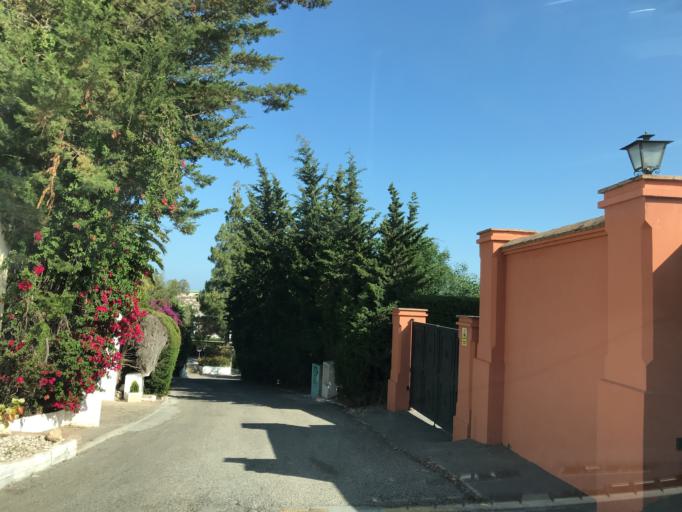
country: ES
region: Andalusia
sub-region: Provincia de Malaga
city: Benahavis
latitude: 36.5033
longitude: -5.0038
